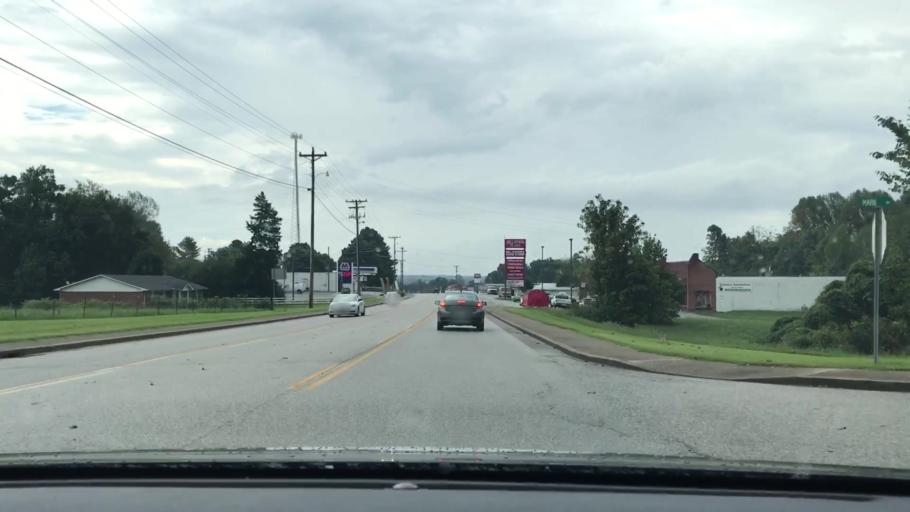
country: US
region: Tennessee
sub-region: Macon County
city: Red Boiling Springs
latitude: 36.5210
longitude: -85.8652
